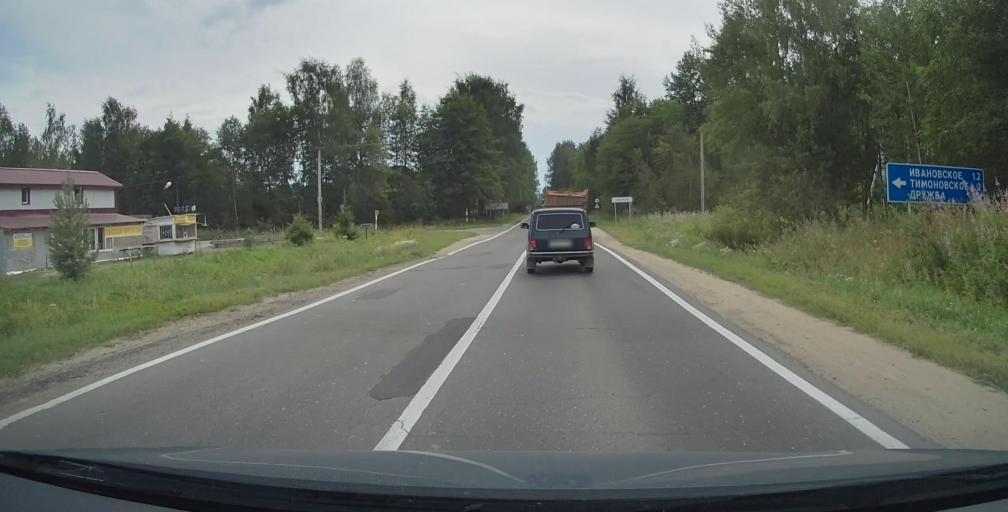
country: RU
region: Jaroslavl
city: Rybinsk
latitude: 58.0017
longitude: 38.7596
